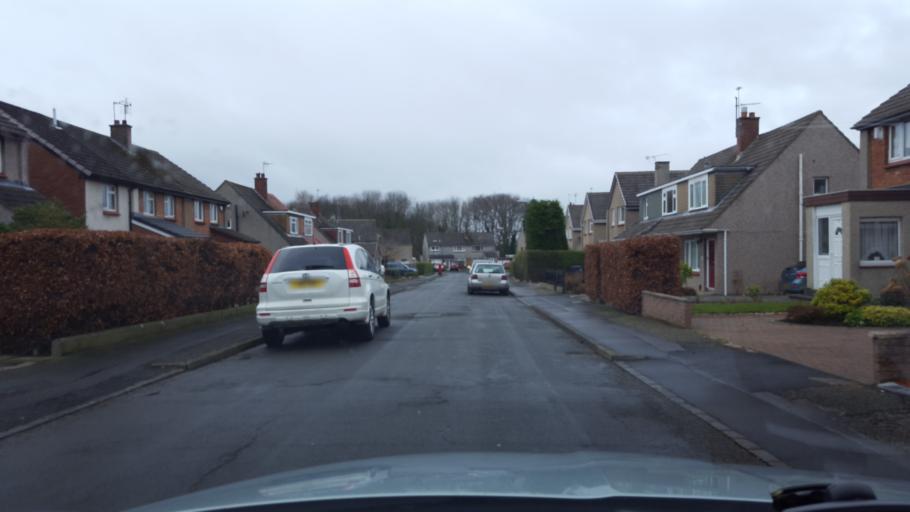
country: GB
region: Scotland
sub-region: Edinburgh
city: Currie
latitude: 55.9022
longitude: -3.2989
